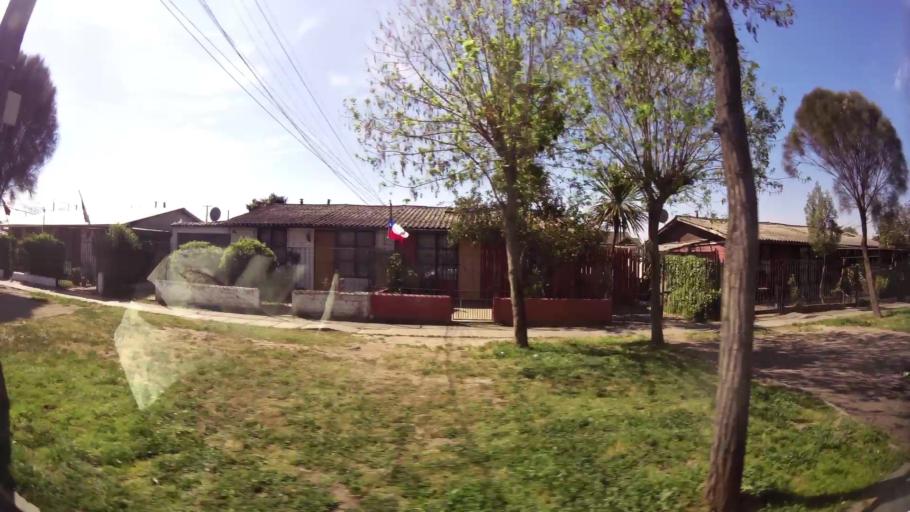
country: CL
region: Santiago Metropolitan
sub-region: Provincia de Santiago
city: Lo Prado
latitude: -33.5039
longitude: -70.7241
